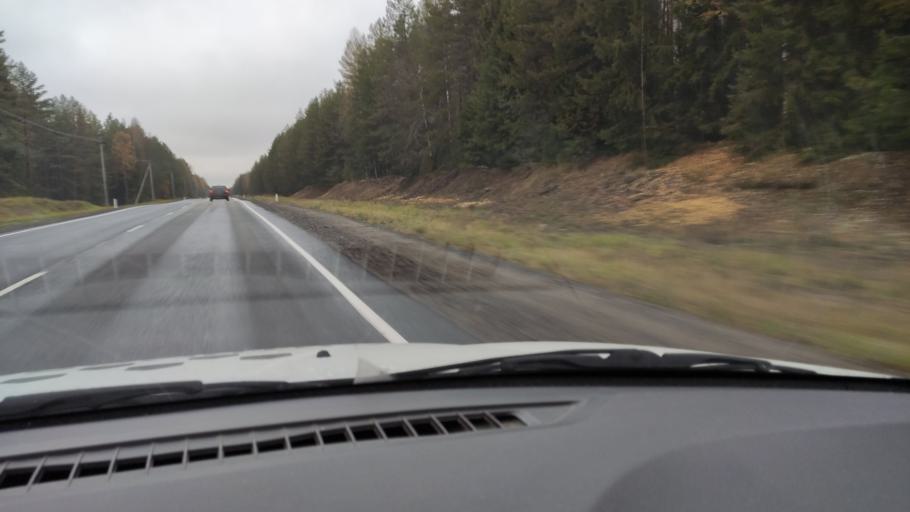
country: RU
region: Kirov
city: Belaya Kholunitsa
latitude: 58.9146
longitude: 51.1575
